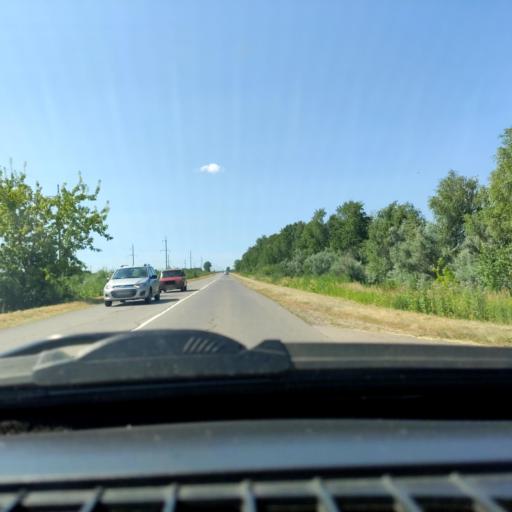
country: RU
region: Samara
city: Tol'yatti
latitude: 53.7286
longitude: 49.4157
